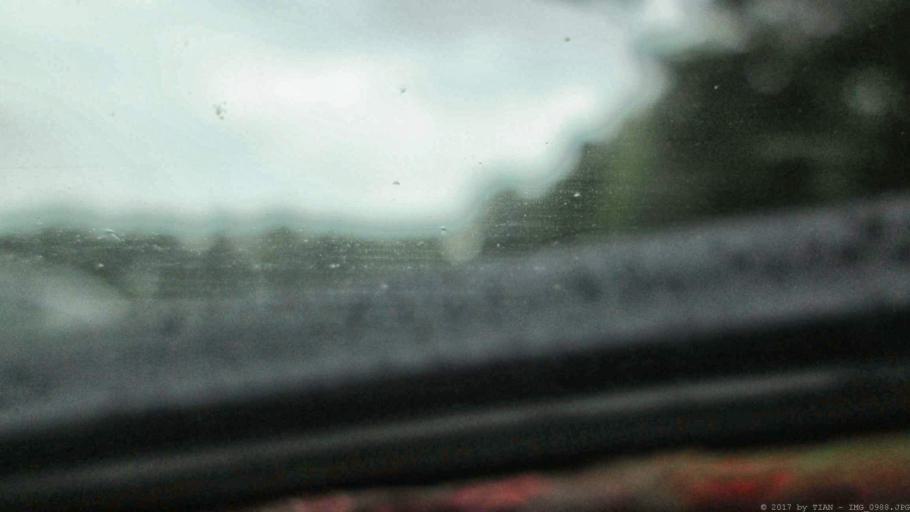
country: DE
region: Lower Saxony
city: Wolfsburg
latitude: 52.4560
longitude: 10.7837
